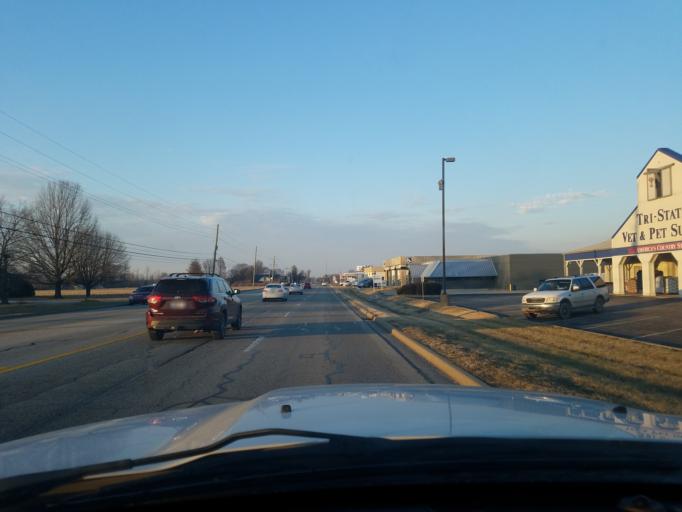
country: US
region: Indiana
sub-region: Vanderburgh County
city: Melody Hill
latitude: 38.0078
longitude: -87.4737
